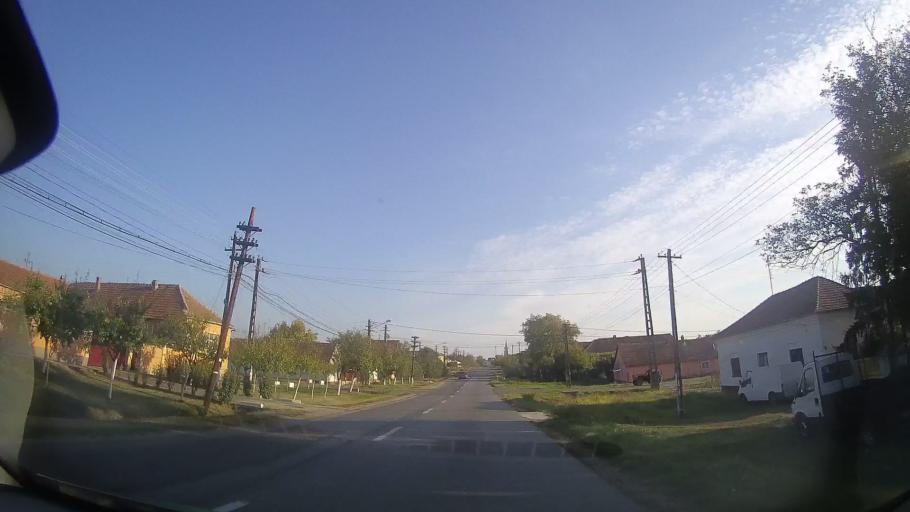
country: RO
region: Timis
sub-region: Comuna Fibis
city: Fibis
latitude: 45.9755
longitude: 21.4237
